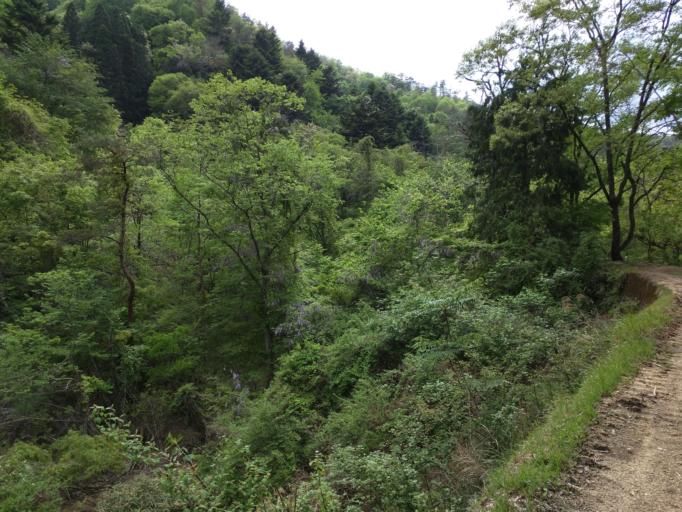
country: JP
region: Mie
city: Ueno-ebisumachi
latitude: 34.8245
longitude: 135.9998
